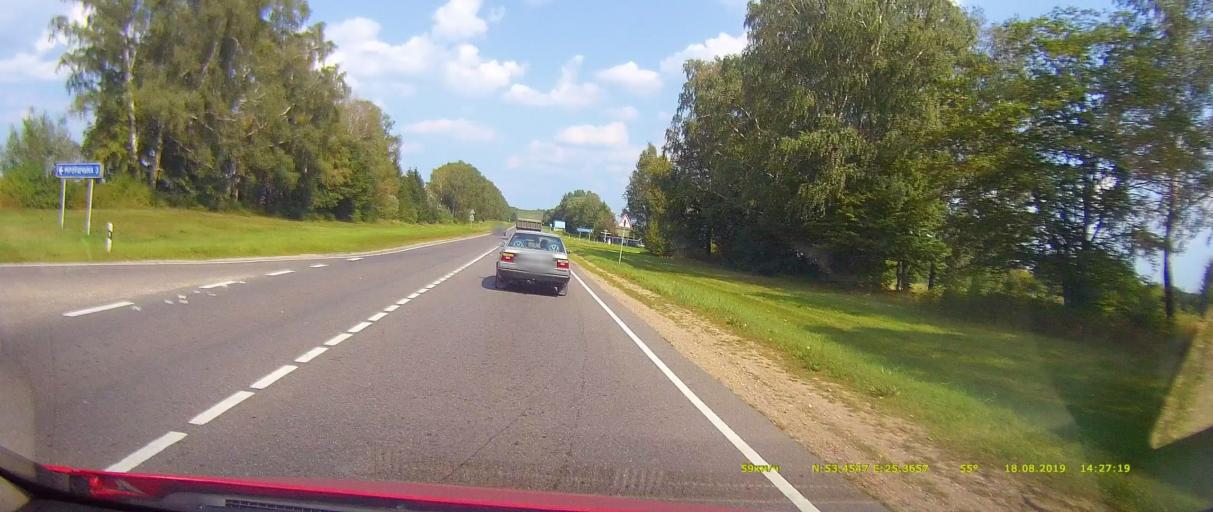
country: BY
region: Grodnenskaya
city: Dzyatlava
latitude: 53.4607
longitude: 25.3818
